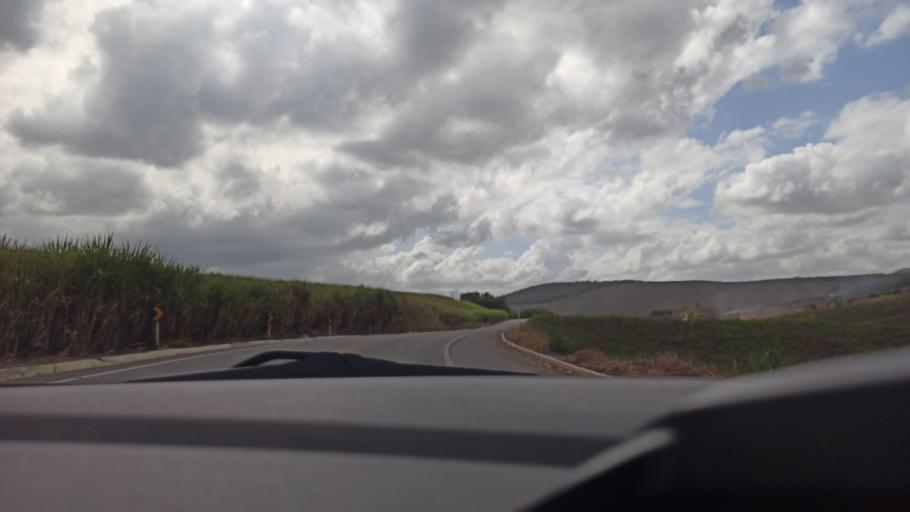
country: BR
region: Pernambuco
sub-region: Timbauba
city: Timbauba
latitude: -7.5408
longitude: -35.2760
